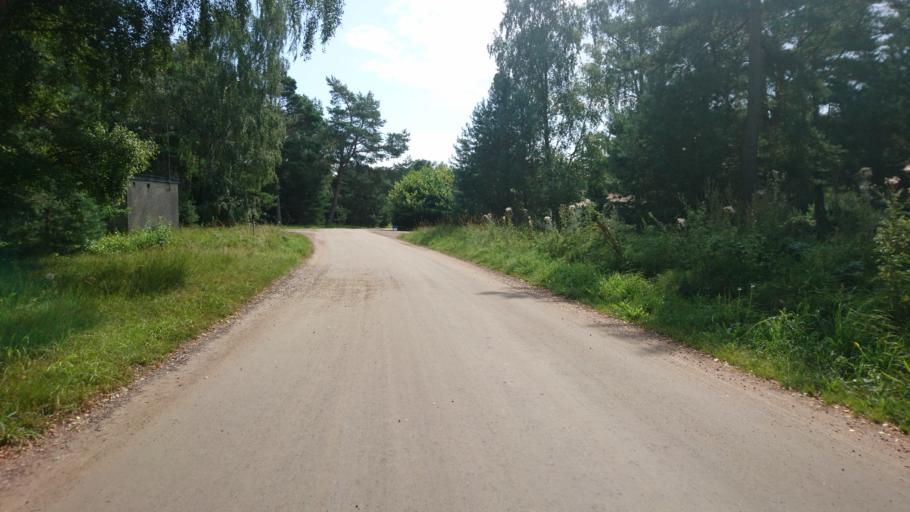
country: SE
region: Skane
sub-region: Vellinge Kommun
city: Ljunghusen
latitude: 55.3979
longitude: 12.9124
